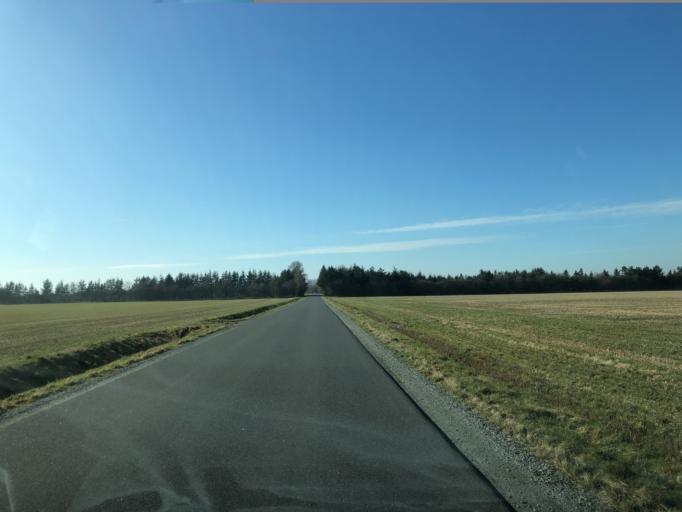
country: DK
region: Central Jutland
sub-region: Ikast-Brande Kommune
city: Bording Kirkeby
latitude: 56.1560
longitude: 9.3200
